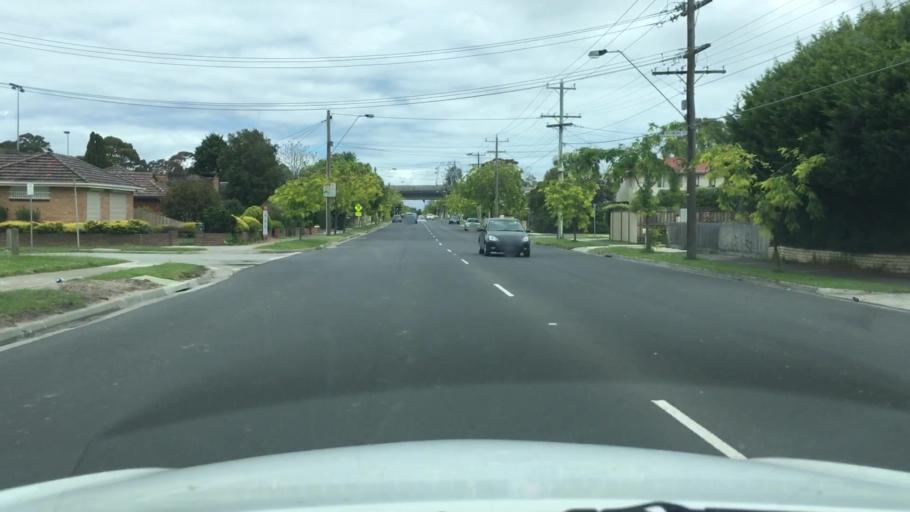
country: AU
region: Victoria
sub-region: Greater Dandenong
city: Noble Park
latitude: -37.9587
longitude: 145.1697
